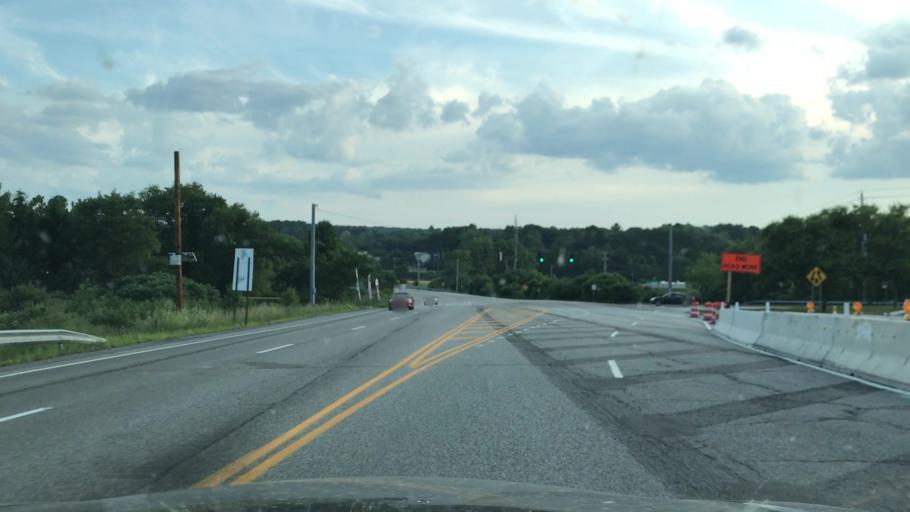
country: US
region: New York
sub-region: Orange County
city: Harriman
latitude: 41.3122
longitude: -74.1400
